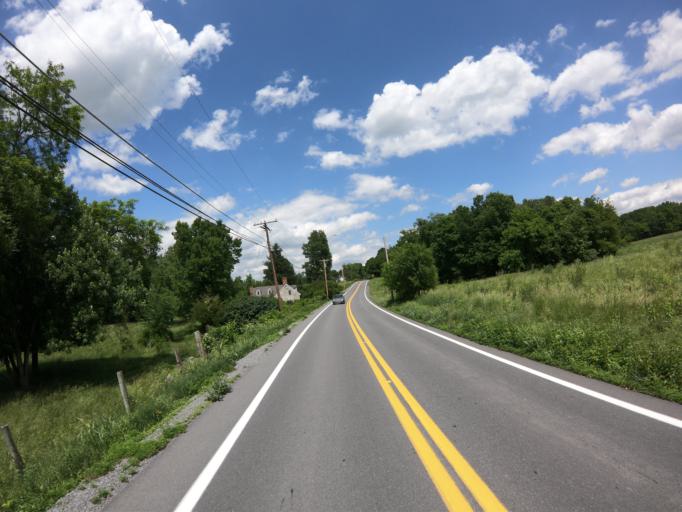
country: US
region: West Virginia
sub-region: Jefferson County
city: Shepherdstown
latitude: 39.3980
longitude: -77.8744
